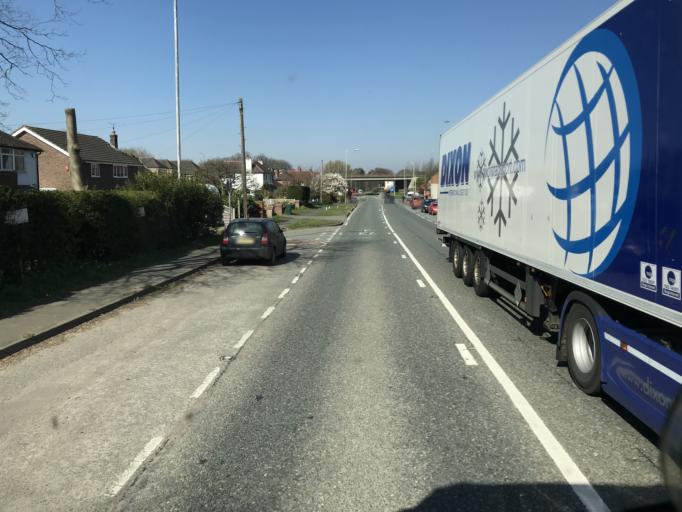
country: GB
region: England
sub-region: Cheshire West and Chester
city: Guilden Sutton
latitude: 53.1837
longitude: -2.8429
